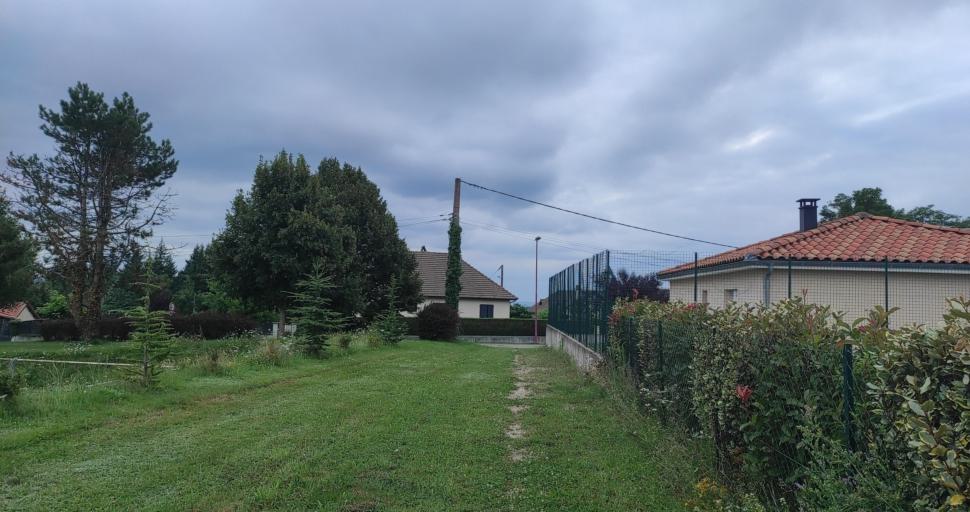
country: FR
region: Midi-Pyrenees
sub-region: Departement de l'Aveyron
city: Villeneuve
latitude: 44.3992
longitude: 2.0733
